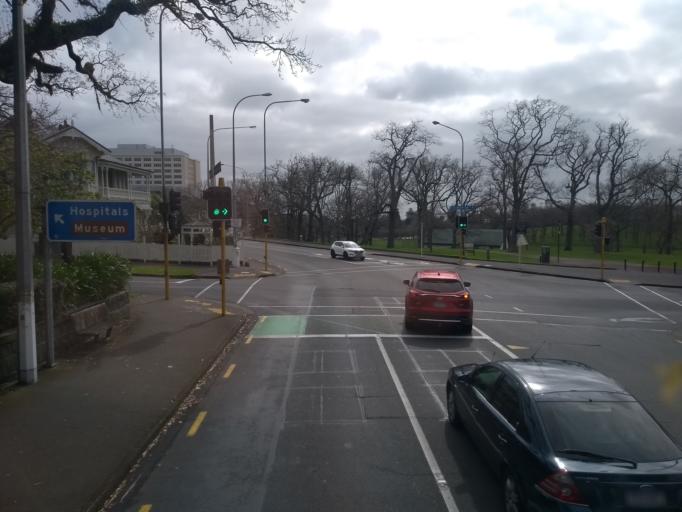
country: NZ
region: Auckland
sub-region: Auckland
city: Auckland
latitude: -36.8643
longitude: 174.7710
